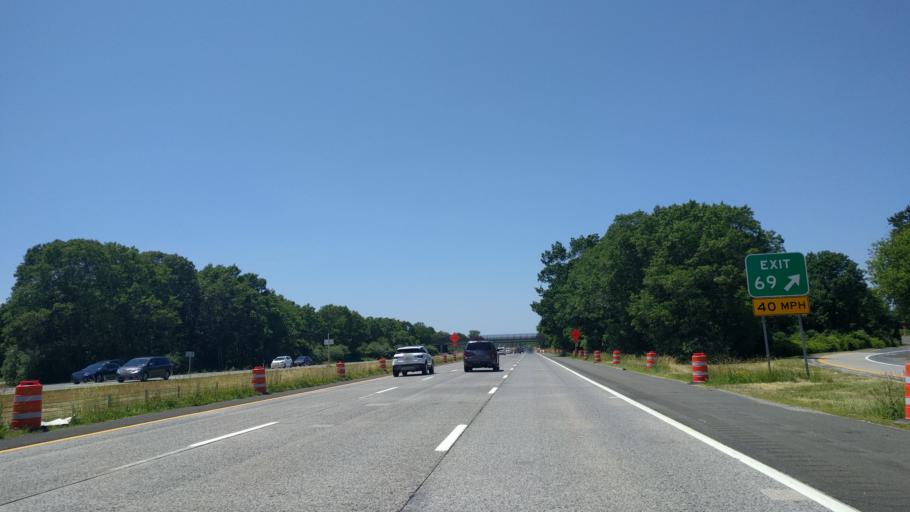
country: US
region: New York
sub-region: Suffolk County
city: Manorville
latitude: 40.8649
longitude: -72.8187
